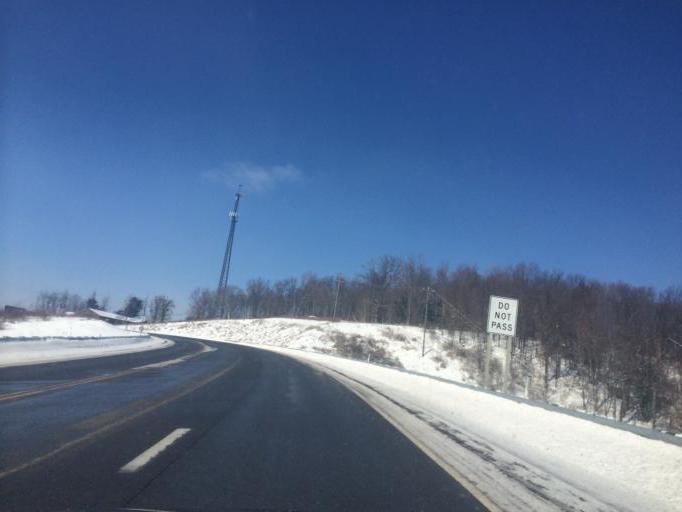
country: US
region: Pennsylvania
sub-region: Centre County
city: Park Forest Village
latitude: 40.8339
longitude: -77.9687
